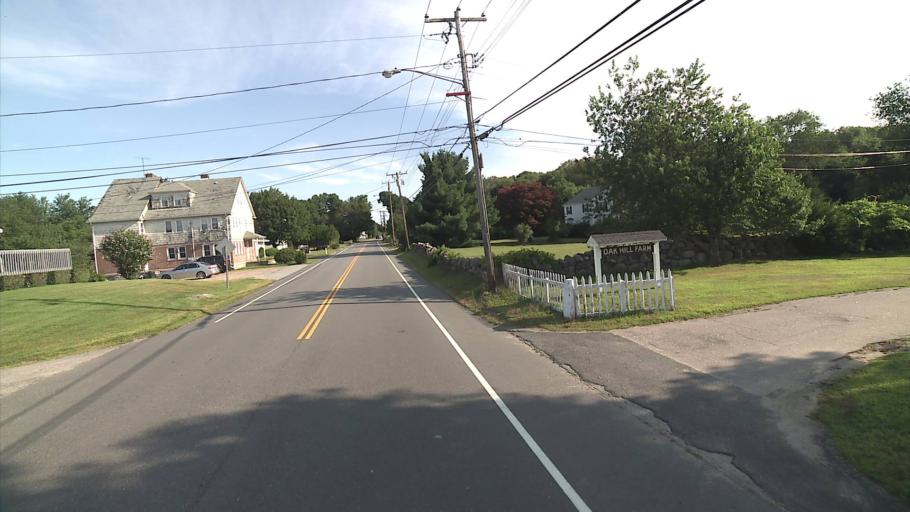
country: US
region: Connecticut
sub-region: New London County
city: Pawcatuck
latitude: 41.3862
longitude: -71.8447
